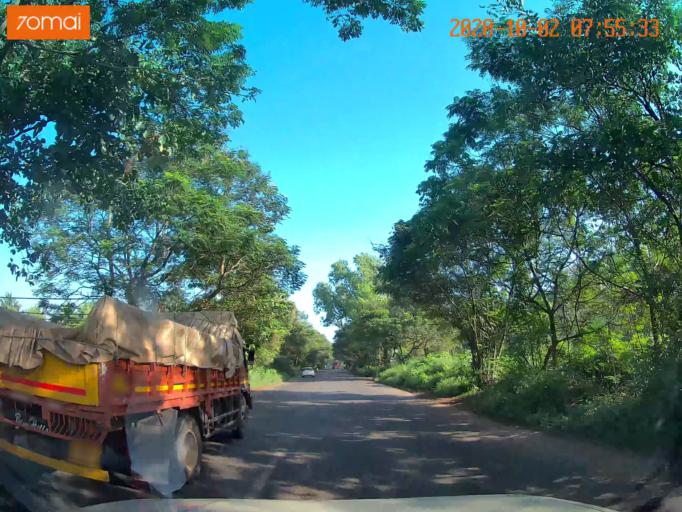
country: IN
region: Kerala
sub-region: Kozhikode
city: Ferokh
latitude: 11.1835
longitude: 75.8715
